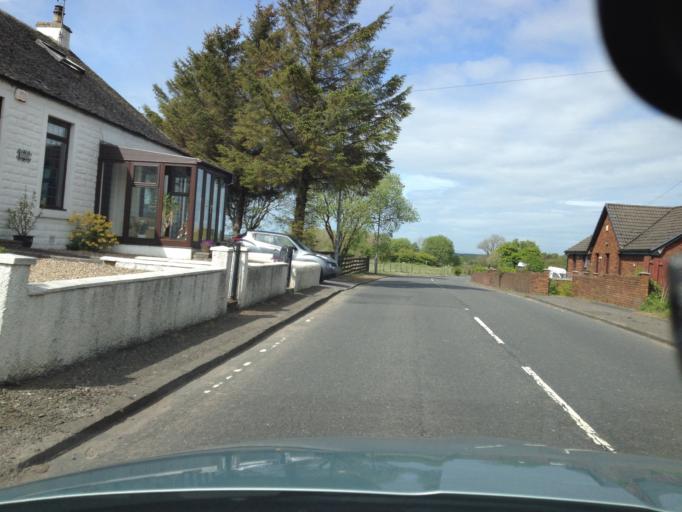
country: GB
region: Scotland
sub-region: West Lothian
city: West Calder
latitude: 55.8543
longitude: -3.5720
